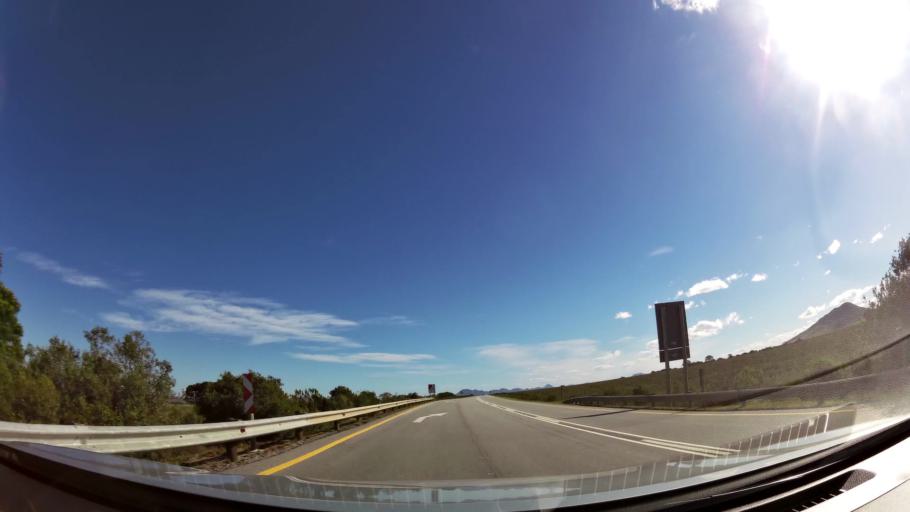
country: ZA
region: Eastern Cape
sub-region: Cacadu District Municipality
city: Kruisfontein
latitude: -34.0099
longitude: 24.6598
